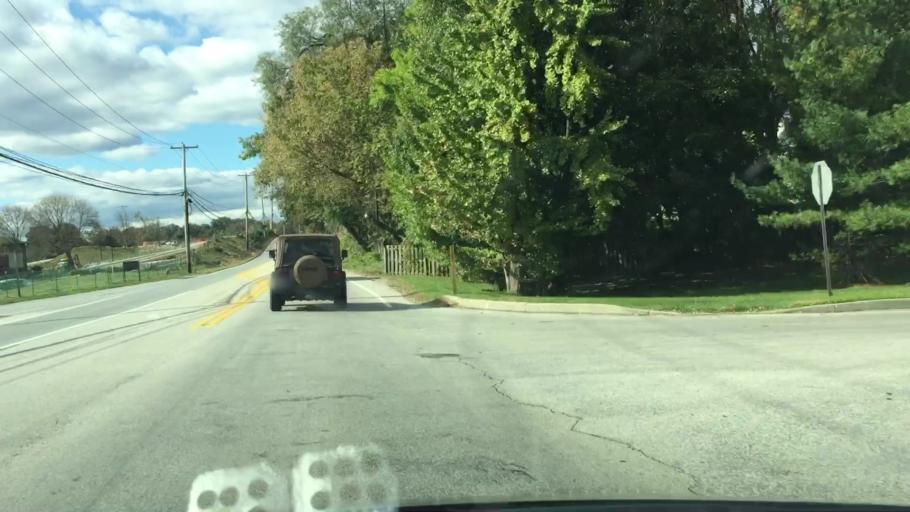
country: US
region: Pennsylvania
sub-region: Chester County
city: Malvern
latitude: 39.9896
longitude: -75.5523
